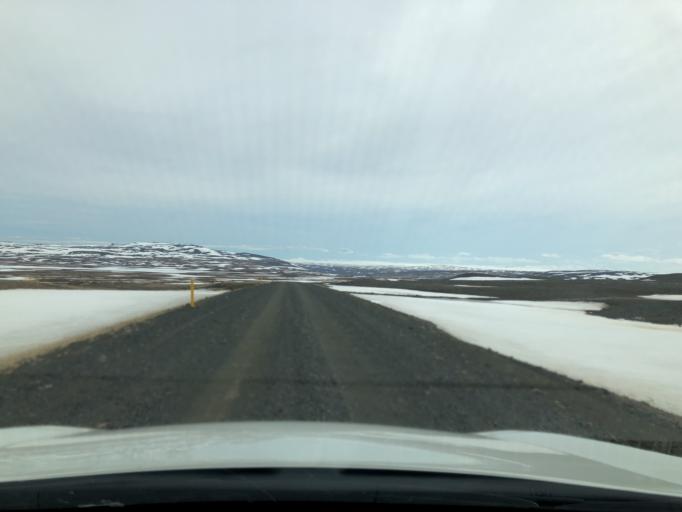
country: IS
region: East
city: Egilsstadir
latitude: 65.3088
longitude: -15.3733
